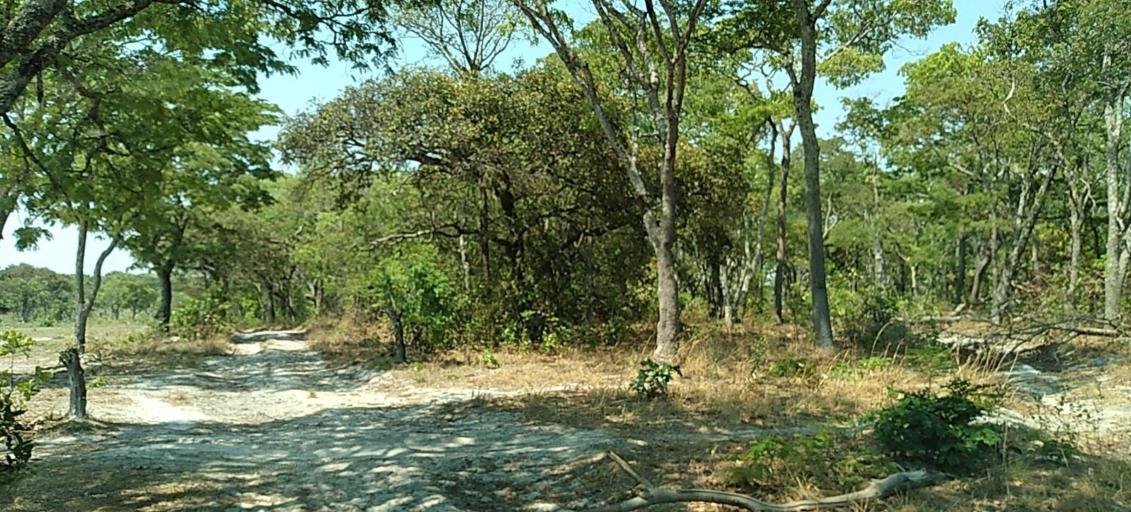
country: ZM
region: Copperbelt
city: Mpongwe
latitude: -13.7823
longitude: 28.1047
